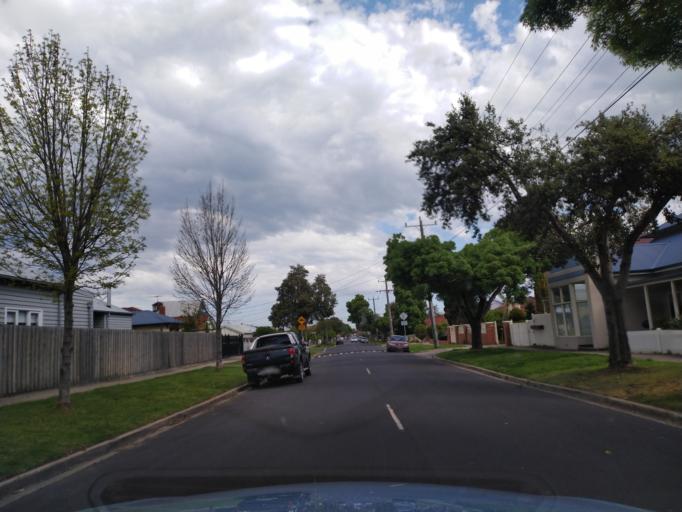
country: AU
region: Victoria
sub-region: Hobsons Bay
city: Newport
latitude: -37.8430
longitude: 144.8732
